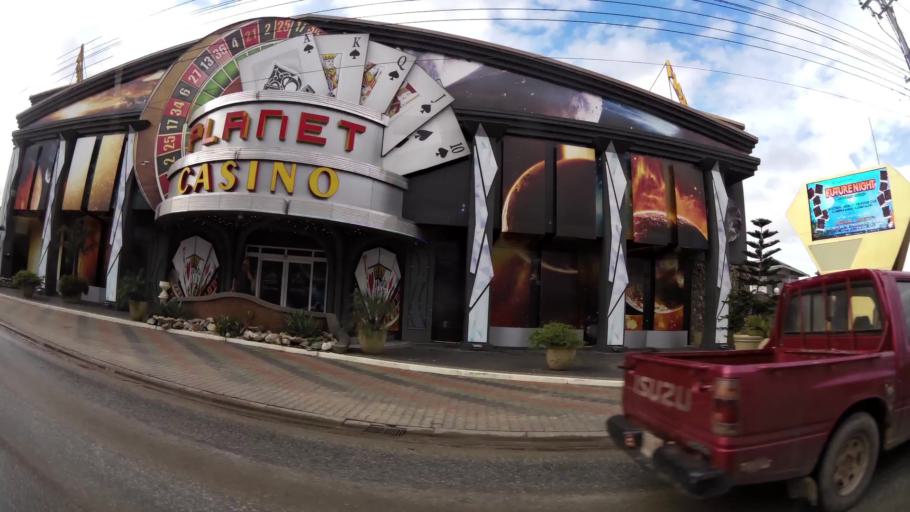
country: SR
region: Paramaribo
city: Paramaribo
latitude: 5.8460
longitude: -55.2285
